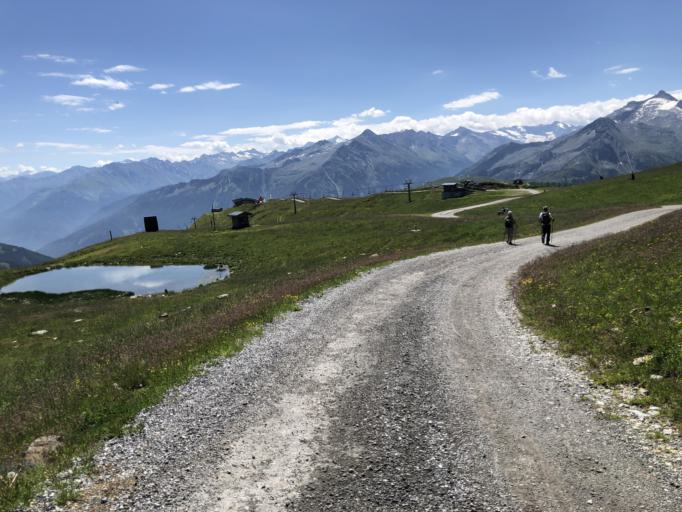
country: AT
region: Salzburg
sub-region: Politischer Bezirk Zell am See
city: Krimml
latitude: 47.2609
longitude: 12.0943
